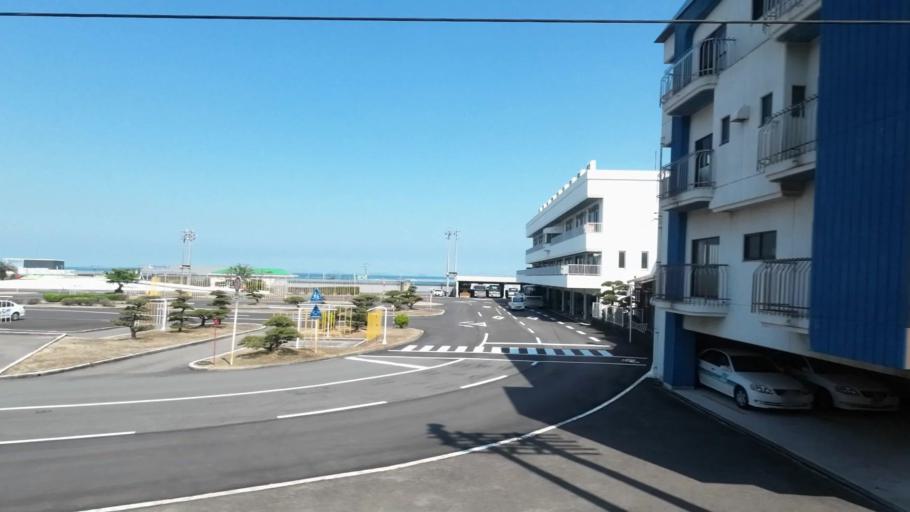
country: JP
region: Ehime
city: Kawanoecho
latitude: 33.9736
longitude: 133.5249
